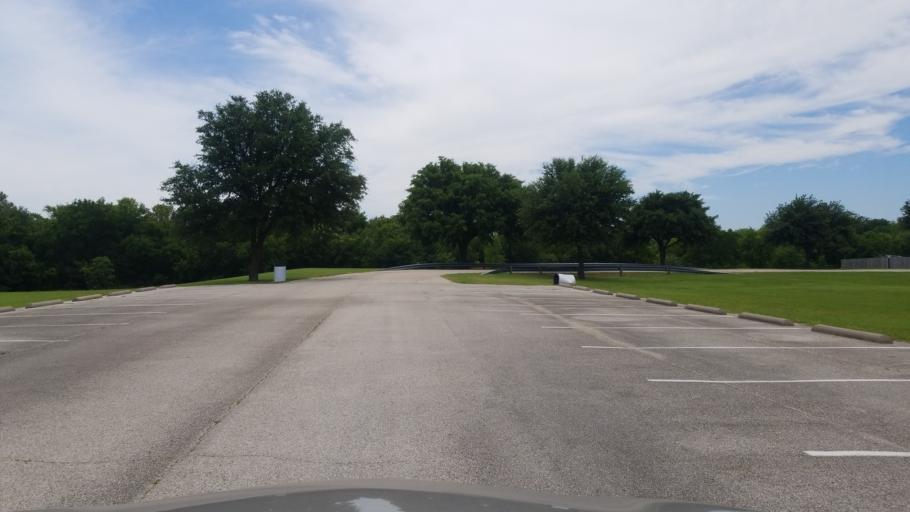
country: US
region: Texas
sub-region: Dallas County
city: Grand Prairie
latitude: 32.6826
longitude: -96.9822
